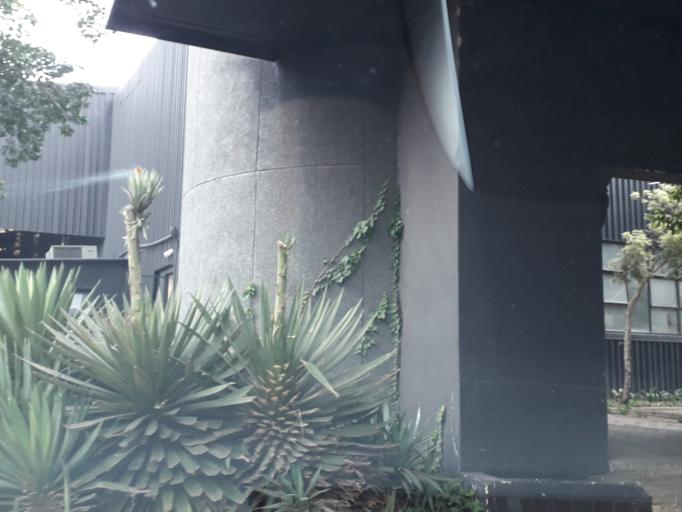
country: ZA
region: Gauteng
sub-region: City of Johannesburg Metropolitan Municipality
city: Modderfontein
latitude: -26.0935
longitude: 28.0840
